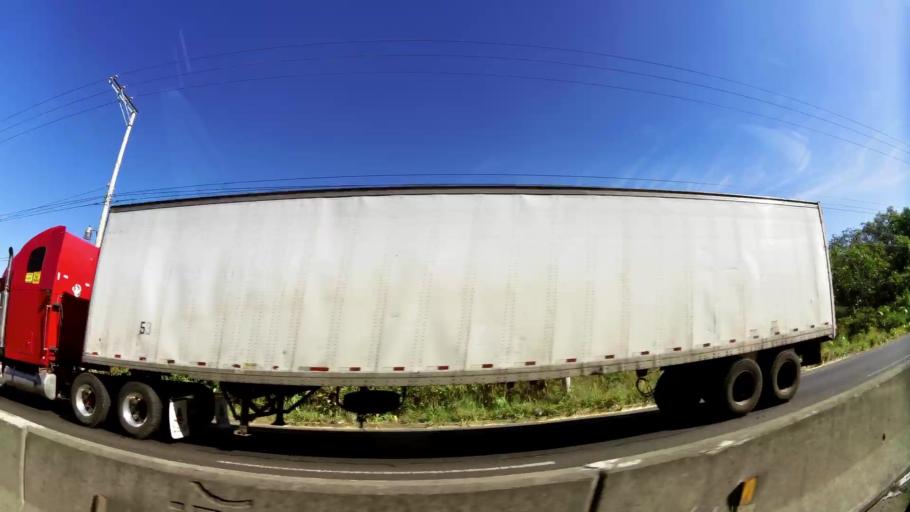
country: SV
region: Santa Ana
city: Coatepeque
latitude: 13.9390
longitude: -89.5307
